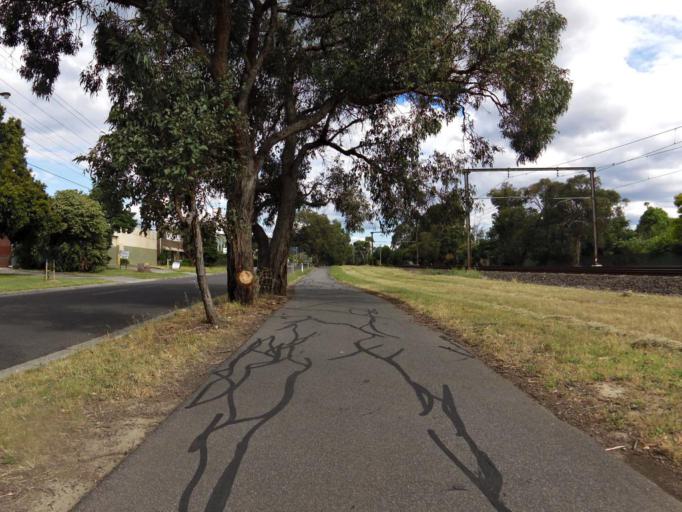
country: AU
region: Victoria
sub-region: Knox
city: Bayswater
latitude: -37.8478
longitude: 145.2743
